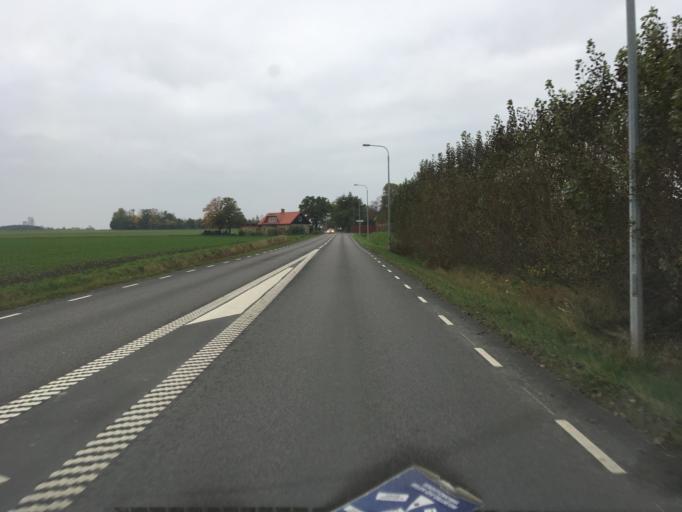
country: SE
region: Skane
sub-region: Lunds Kommun
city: Lund
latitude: 55.7425
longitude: 13.1991
